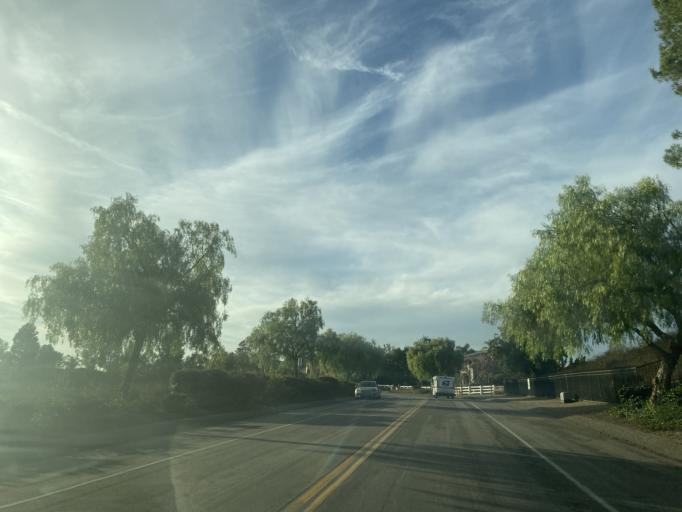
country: US
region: California
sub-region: Orange County
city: Brea
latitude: 33.8945
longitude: -117.8987
